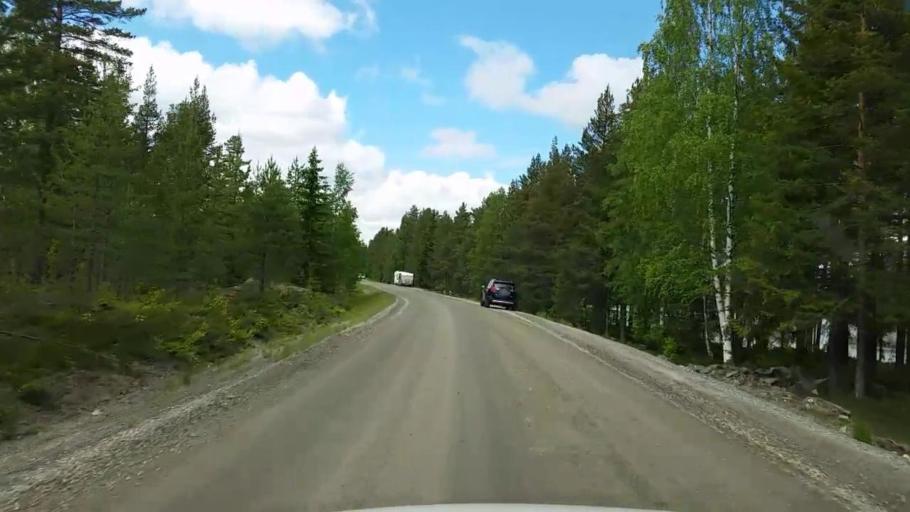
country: SE
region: Gaevleborg
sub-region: Bollnas Kommun
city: Kilafors
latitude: 61.0189
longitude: 16.3814
